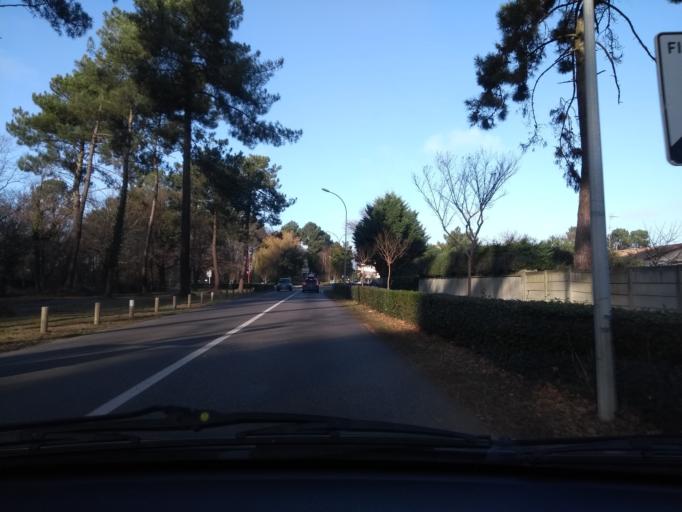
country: FR
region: Aquitaine
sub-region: Departement de la Gironde
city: Gujan-Mestras
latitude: 44.6213
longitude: -1.0731
